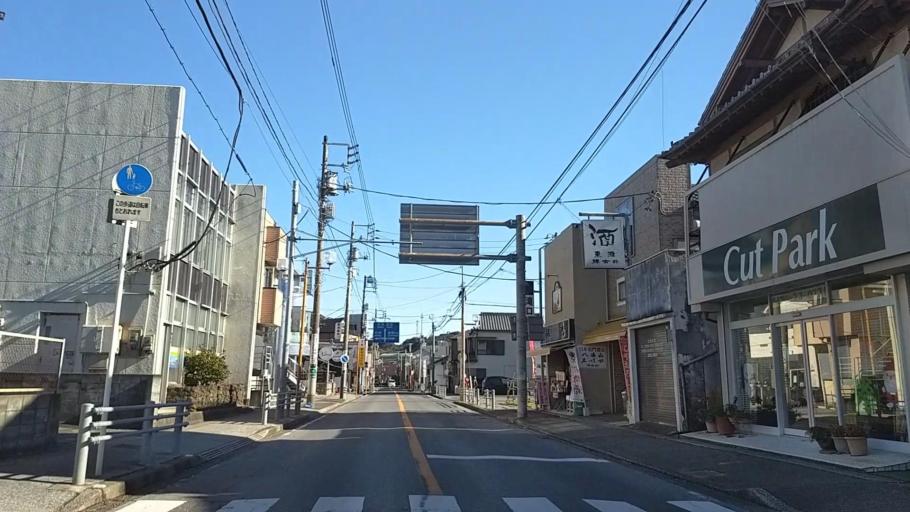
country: JP
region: Chiba
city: Katsuura
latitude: 35.1505
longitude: 140.3114
